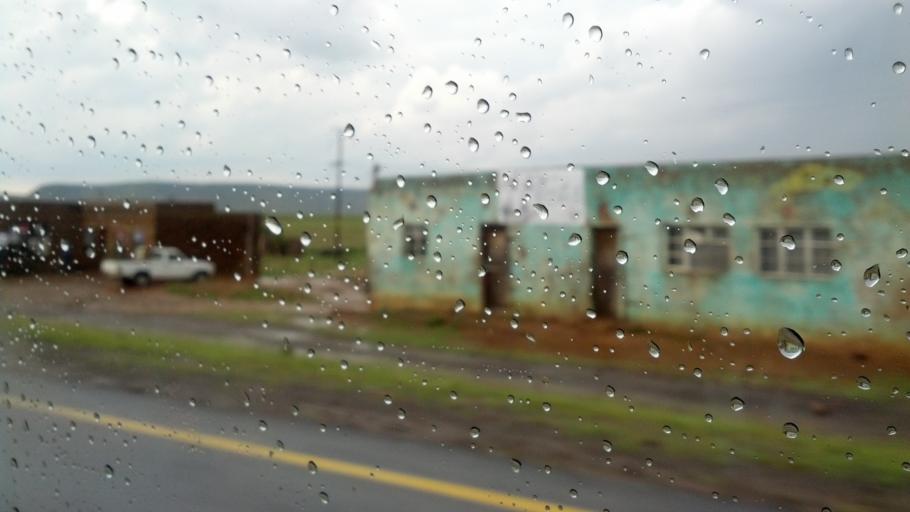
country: LS
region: Mafeteng
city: Mafeteng
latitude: -29.7547
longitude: 27.1302
